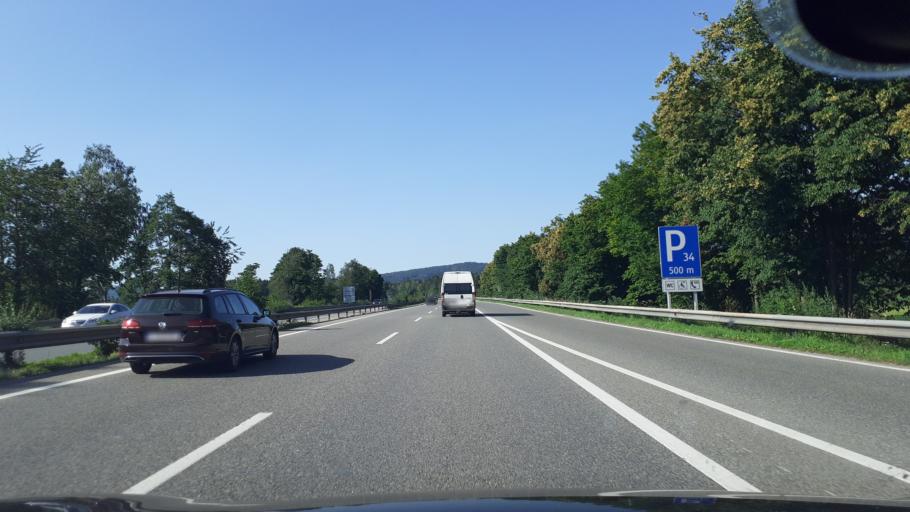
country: AT
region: Vorarlberg
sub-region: Politischer Bezirk Feldkirch
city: Rankweil
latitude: 47.2834
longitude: 9.6248
